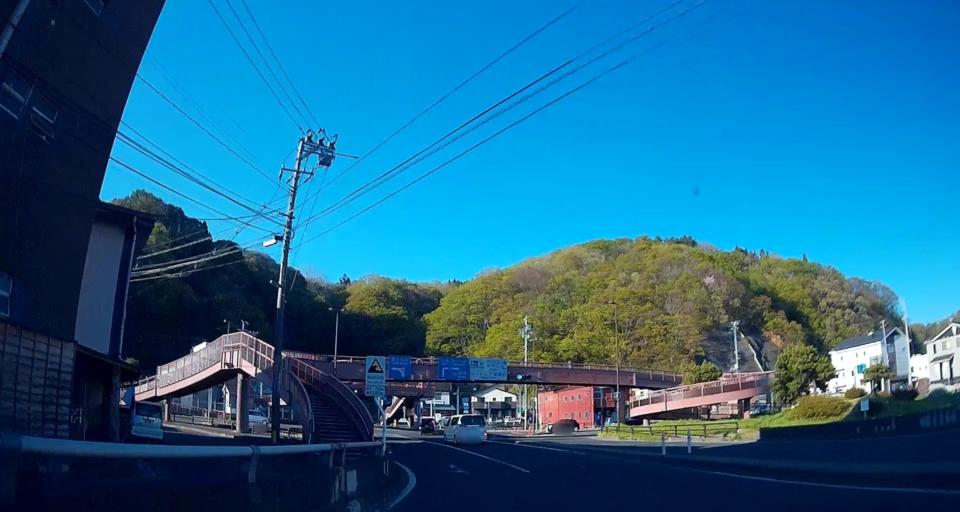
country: JP
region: Iwate
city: Miyako
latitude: 39.6417
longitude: 141.9566
